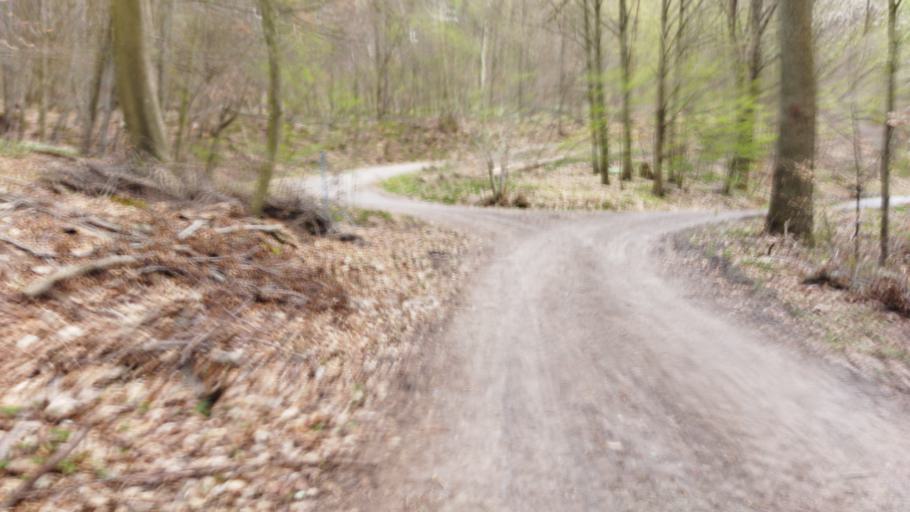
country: DE
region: Baden-Wuerttemberg
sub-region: Regierungsbezirk Stuttgart
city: Eberstadt
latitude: 49.2023
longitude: 9.2995
